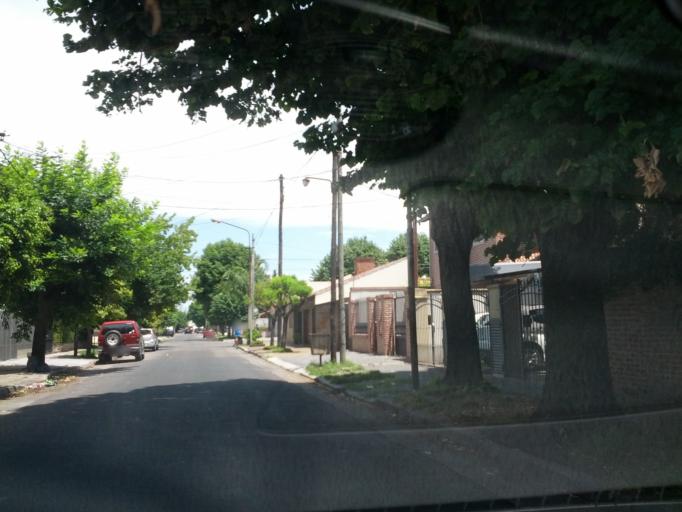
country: AR
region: Buenos Aires
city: San Justo
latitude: -34.6475
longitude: -58.5727
